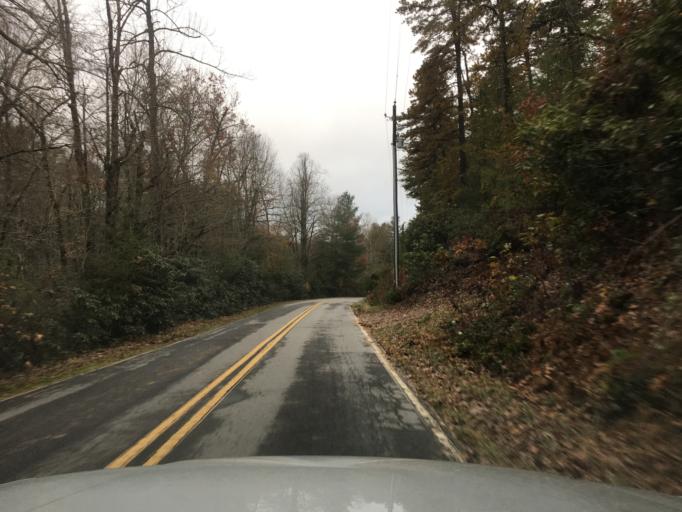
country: US
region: North Carolina
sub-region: Rutherford County
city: Lake Lure
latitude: 35.5339
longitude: -82.2353
